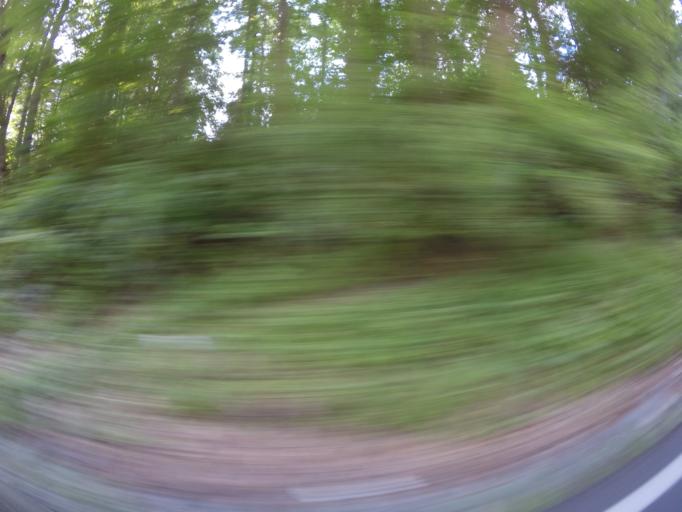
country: US
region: Maryland
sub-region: Harford County
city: Joppatowne
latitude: 39.4741
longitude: -76.3353
